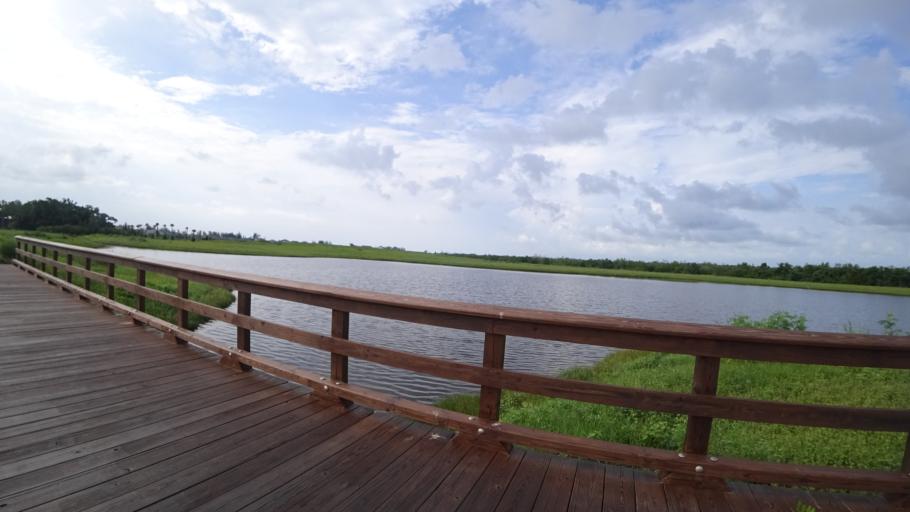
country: US
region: Florida
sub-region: Manatee County
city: Cortez
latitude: 27.5067
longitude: -82.6673
